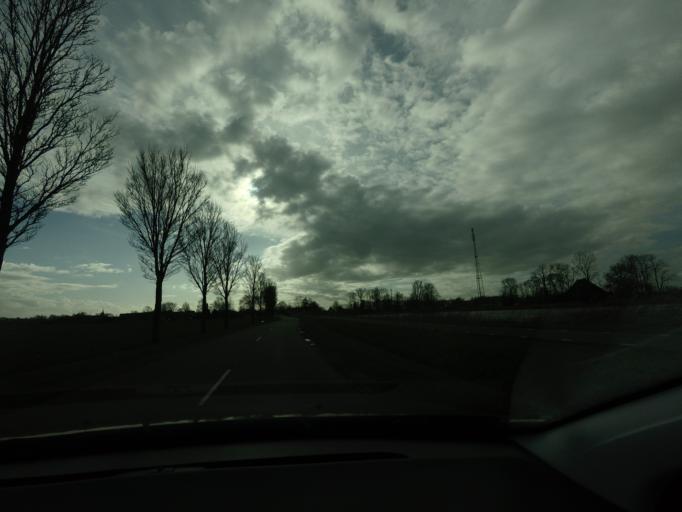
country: NL
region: Friesland
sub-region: Gemeente Boarnsterhim
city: Jirnsum
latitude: 53.0846
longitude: 5.7992
